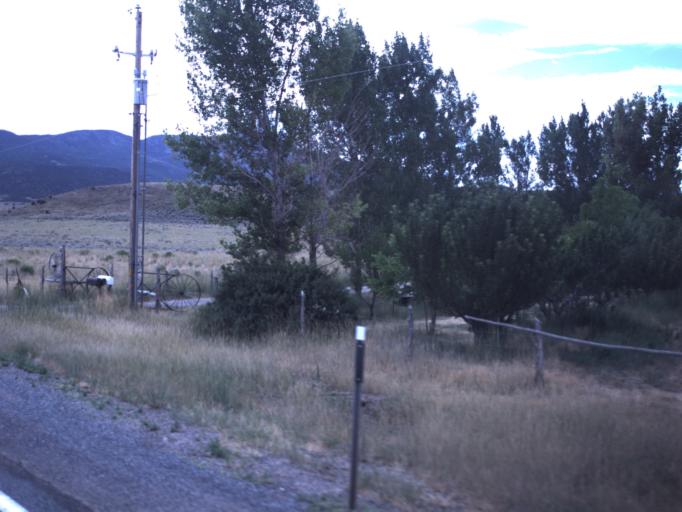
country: US
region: Utah
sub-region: Beaver County
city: Beaver
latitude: 38.6072
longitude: -112.5908
